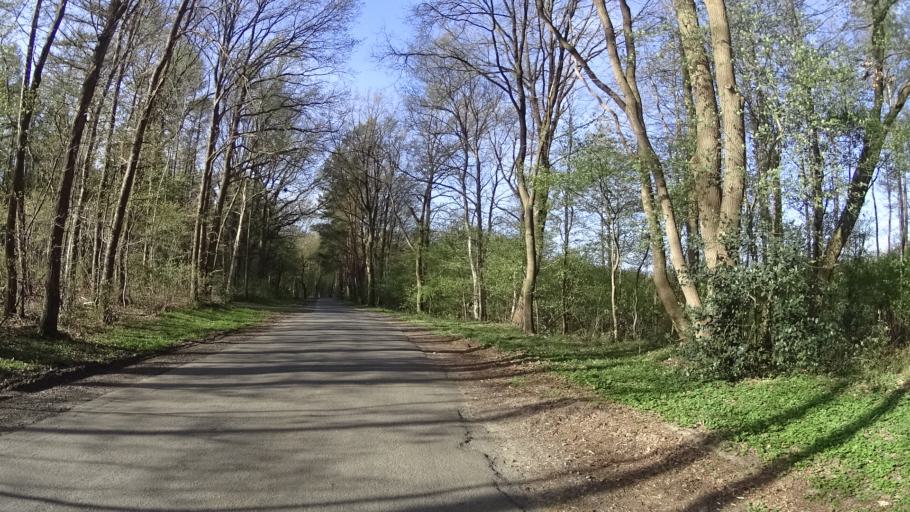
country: DE
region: Lower Saxony
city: Haren
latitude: 52.7680
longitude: 7.2676
